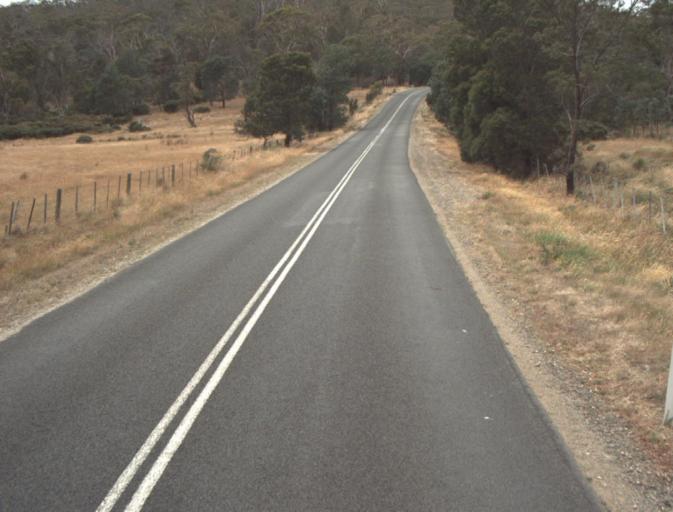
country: AU
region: Tasmania
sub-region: Northern Midlands
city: Evandale
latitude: -41.5096
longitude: 147.3173
